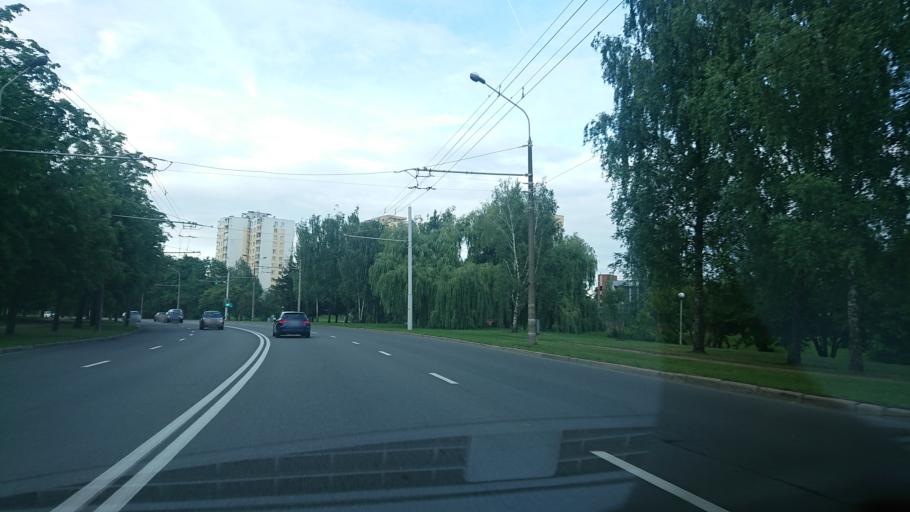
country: BY
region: Minsk
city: Borovlyany
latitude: 53.9379
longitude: 27.6426
